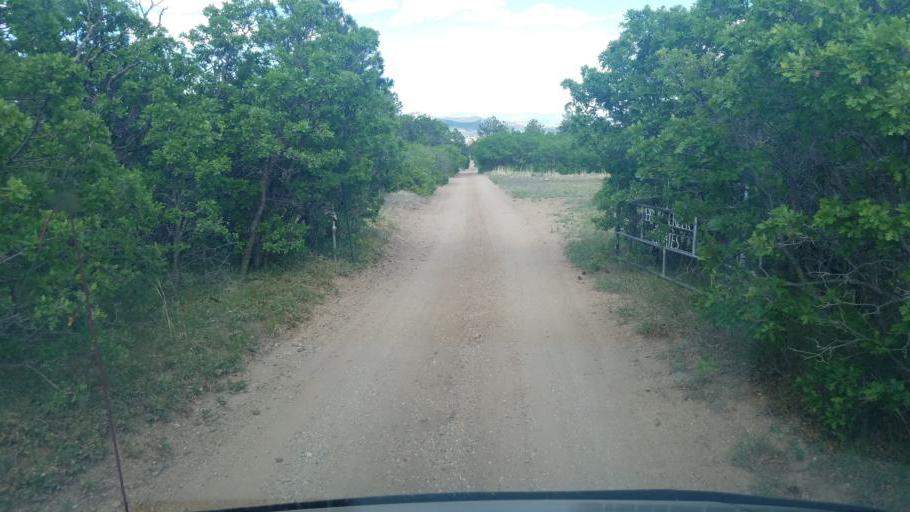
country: US
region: Colorado
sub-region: Custer County
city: Westcliffe
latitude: 38.2218
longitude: -105.6150
